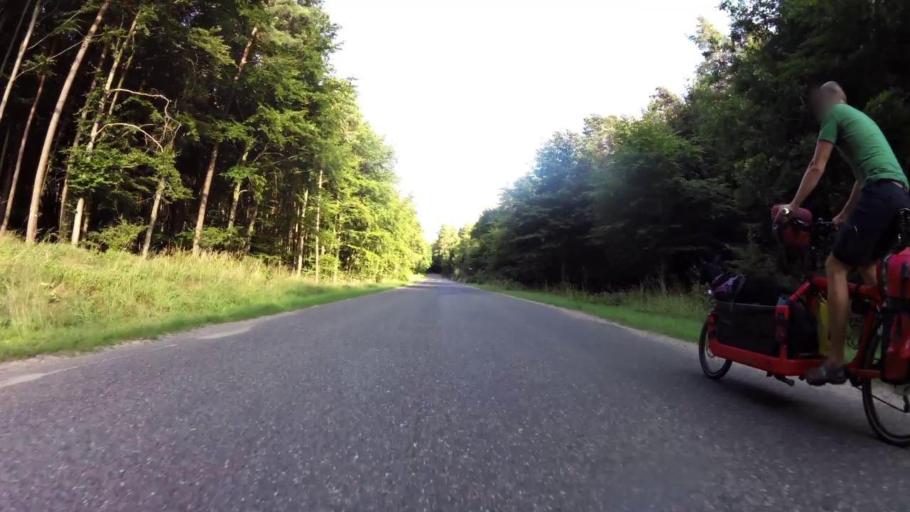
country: PL
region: West Pomeranian Voivodeship
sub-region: Powiat drawski
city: Drawsko Pomorskie
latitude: 53.4704
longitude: 15.8327
